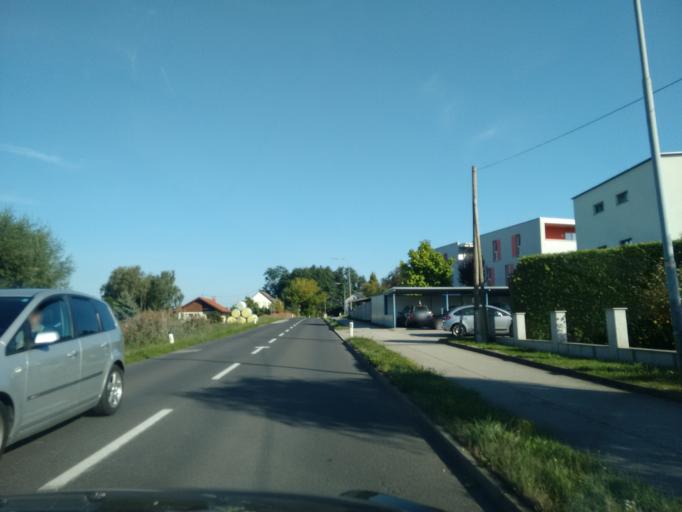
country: AT
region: Upper Austria
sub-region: Politischer Bezirk Linz-Land
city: Traun
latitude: 48.1436
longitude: 14.2238
